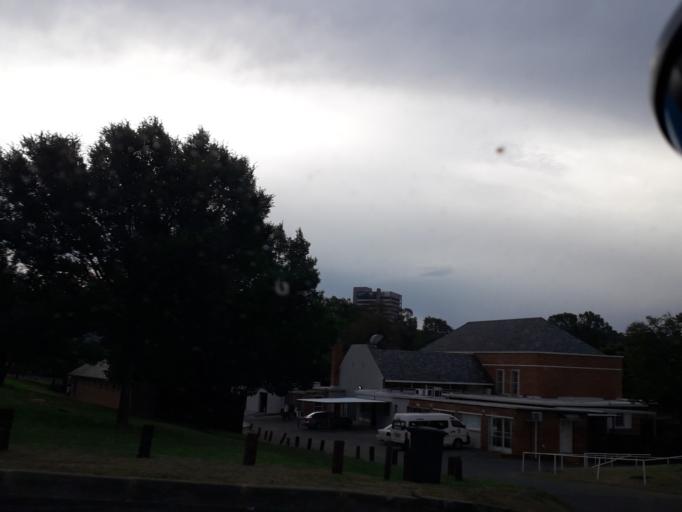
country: ZA
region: Gauteng
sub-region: City of Johannesburg Metropolitan Municipality
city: Johannesburg
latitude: -26.0878
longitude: 28.0155
